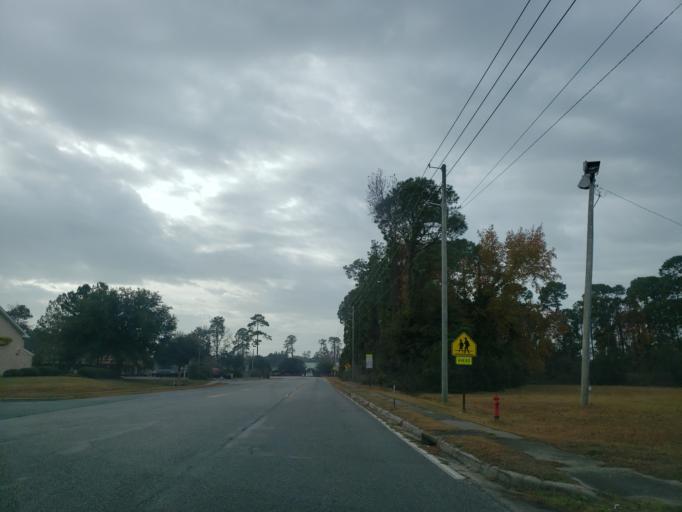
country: US
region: Georgia
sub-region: Chatham County
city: Whitemarsh Island
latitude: 32.0424
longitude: -81.0102
